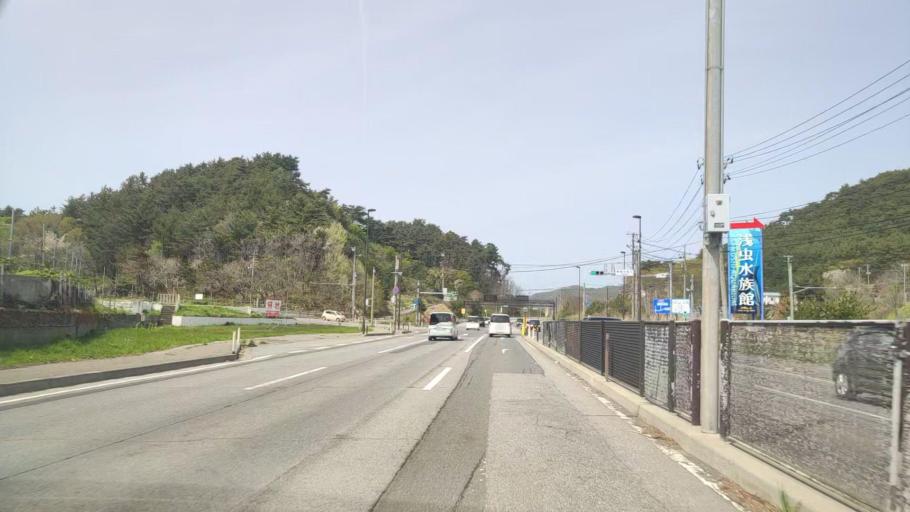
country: JP
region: Aomori
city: Aomori Shi
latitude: 40.8994
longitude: 140.8605
